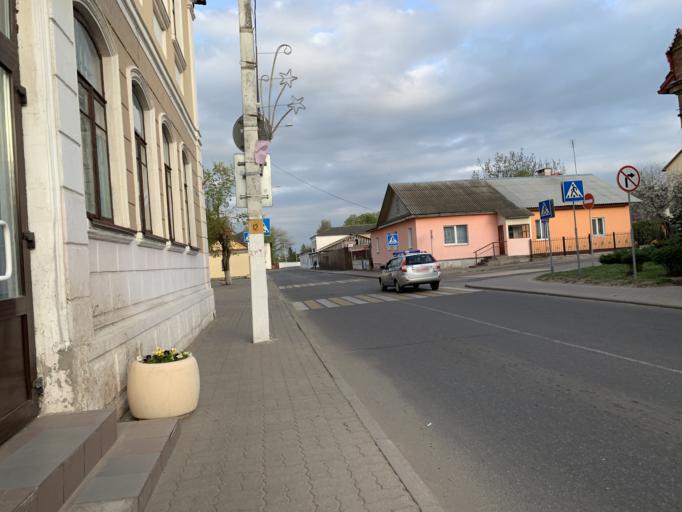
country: BY
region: Minsk
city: Nyasvizh
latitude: 53.2208
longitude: 26.6812
